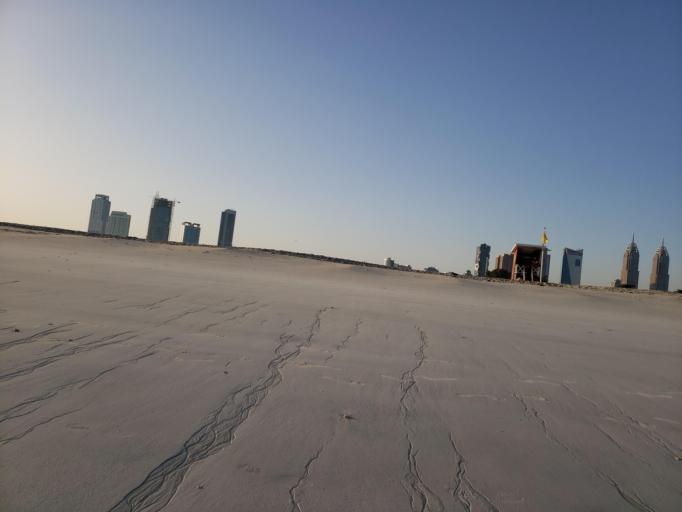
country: AE
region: Dubai
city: Dubai
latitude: 25.1163
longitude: 55.1655
